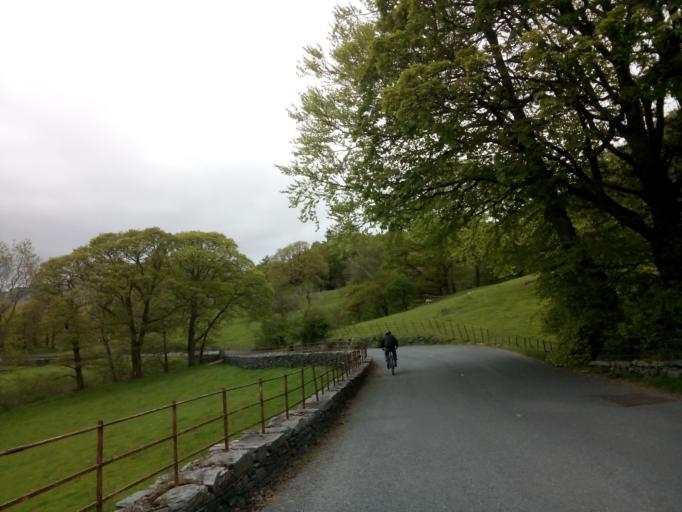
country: GB
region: England
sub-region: Cumbria
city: Ambleside
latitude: 54.4304
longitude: -3.0225
